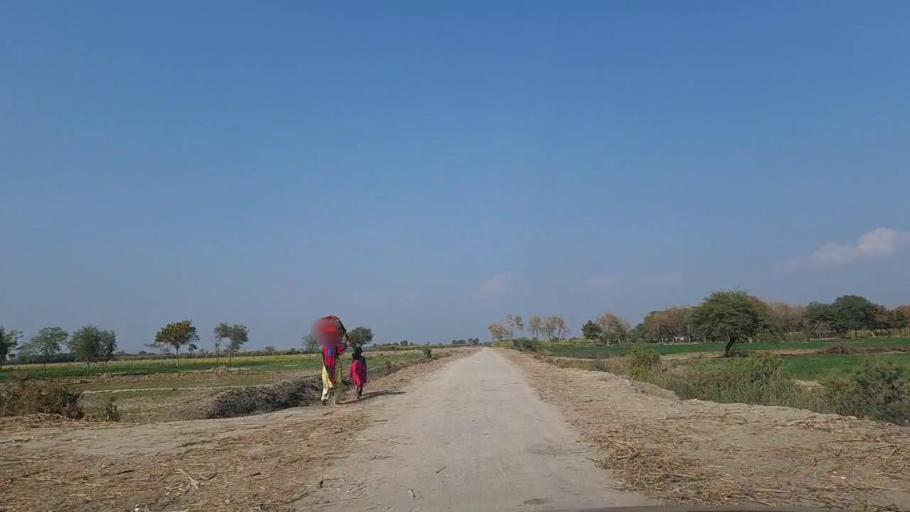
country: PK
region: Sindh
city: Jam Sahib
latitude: 26.2982
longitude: 68.5832
